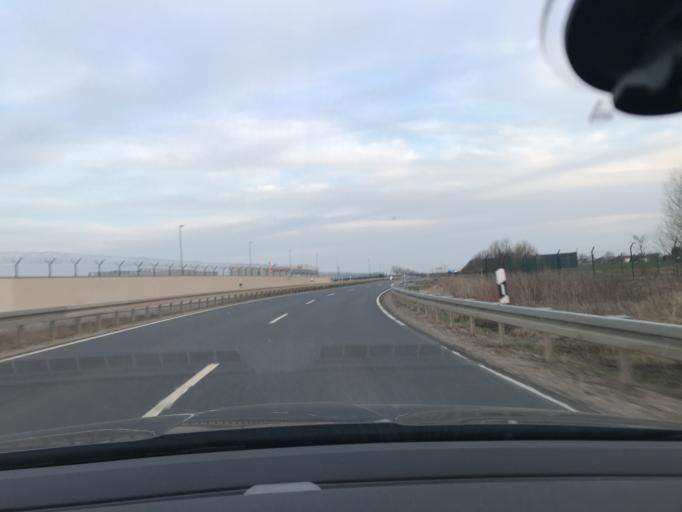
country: DE
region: Brandenburg
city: Schonefeld
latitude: 52.3622
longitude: 13.4764
